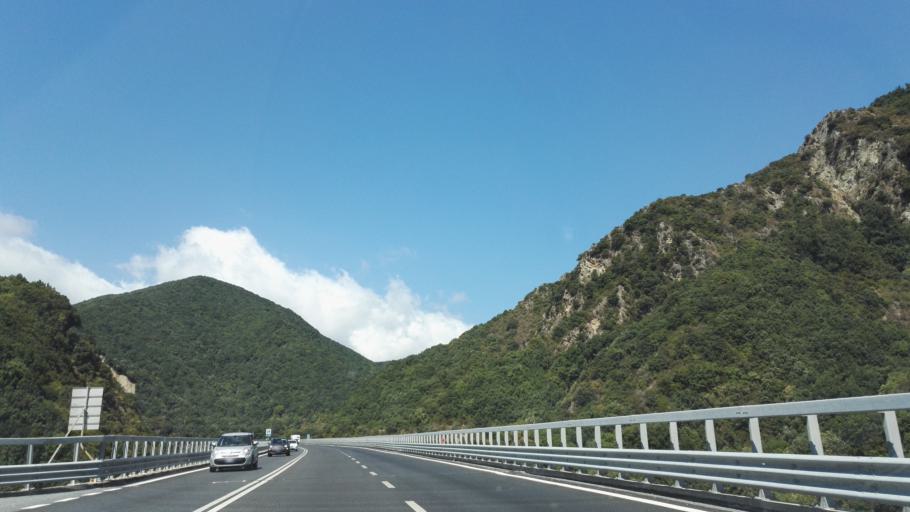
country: IT
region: Calabria
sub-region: Provincia di Reggio Calabria
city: Mammola
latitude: 38.3616
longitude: 16.1990
